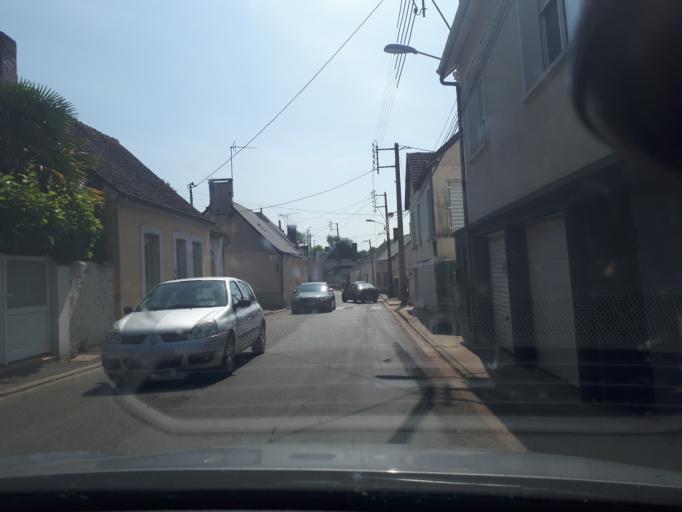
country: FR
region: Pays de la Loire
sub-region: Departement de la Sarthe
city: Montfort-le-Gesnois
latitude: 48.0484
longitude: 0.4012
